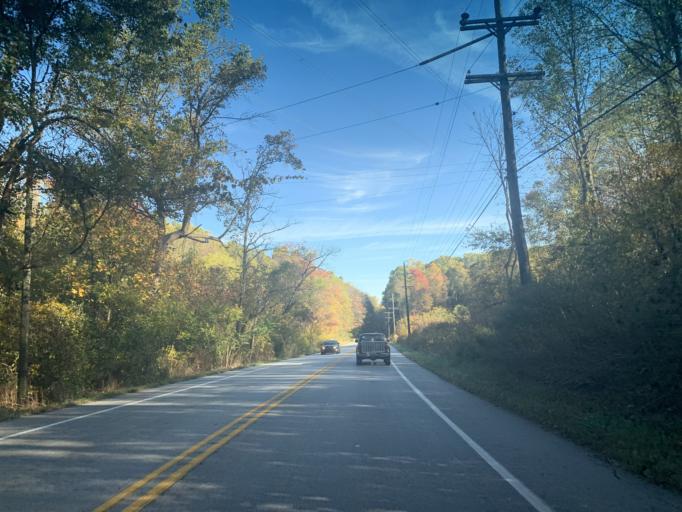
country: US
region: Pennsylvania
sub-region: Chester County
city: Parkesburg
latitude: 39.9465
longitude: -75.9150
